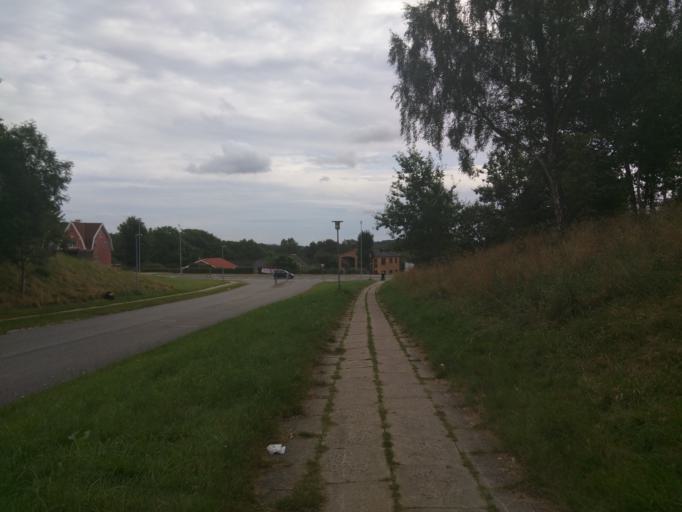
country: DK
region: Central Jutland
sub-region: Viborg Kommune
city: Viborg
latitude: 56.4357
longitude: 9.3942
